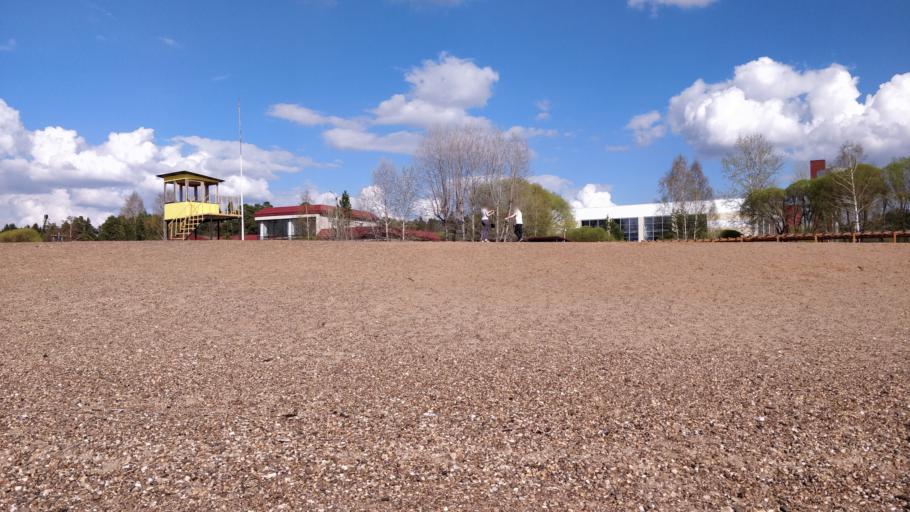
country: RU
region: Perm
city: Ust'-Kachka
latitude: 58.0126
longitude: 55.6684
